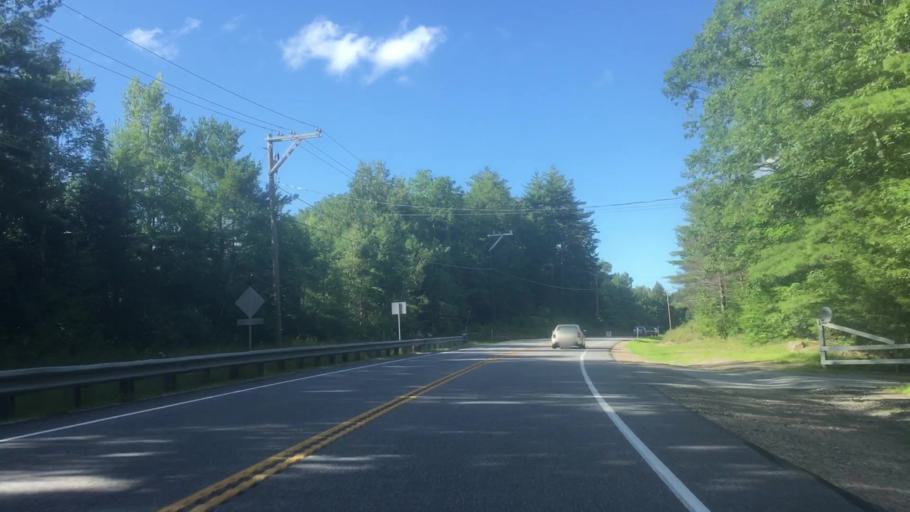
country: US
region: New Hampshire
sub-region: Hillsborough County
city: Hillsborough
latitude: 43.1082
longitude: -71.9568
